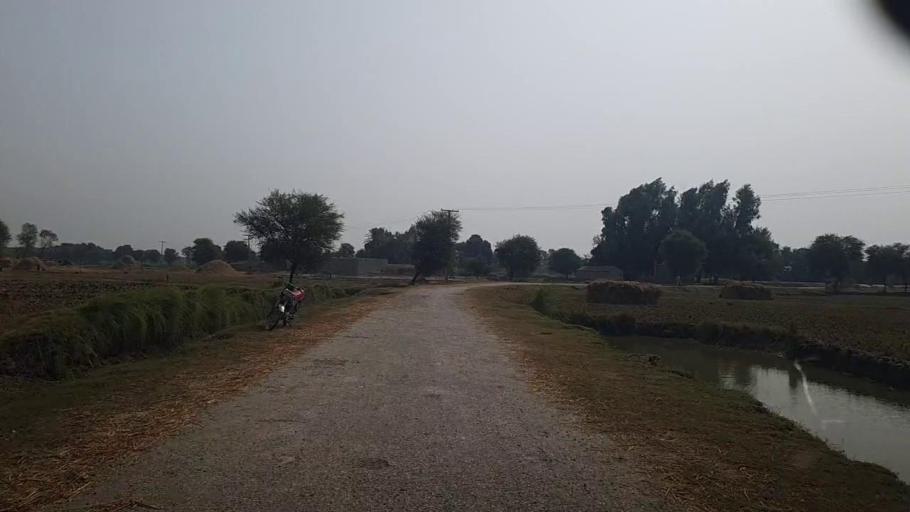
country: PK
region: Sindh
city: Kashmor
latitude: 28.3797
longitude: 69.4456
